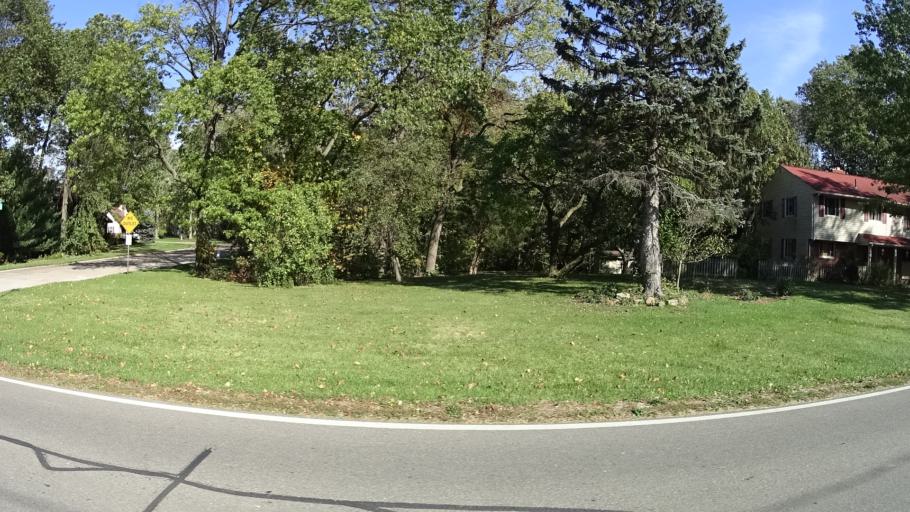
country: US
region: Ohio
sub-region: Lorain County
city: Vermilion
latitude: 41.4116
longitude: -82.3475
